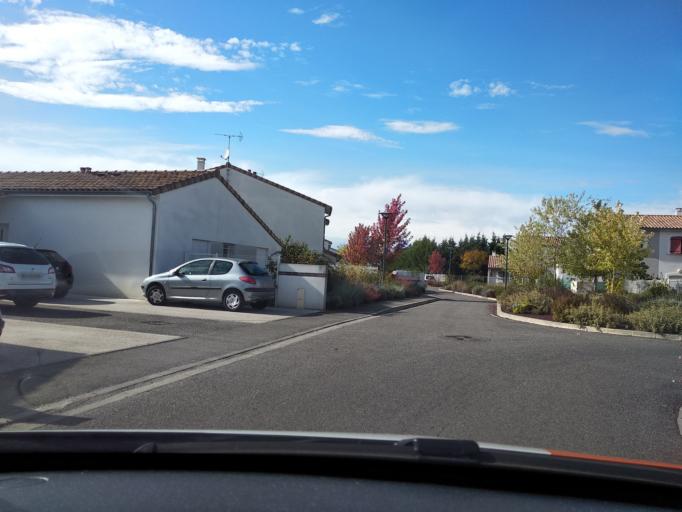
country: FR
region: Midi-Pyrenees
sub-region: Departement du Tarn-et-Garonne
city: Montauban
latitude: 44.0439
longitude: 1.3305
